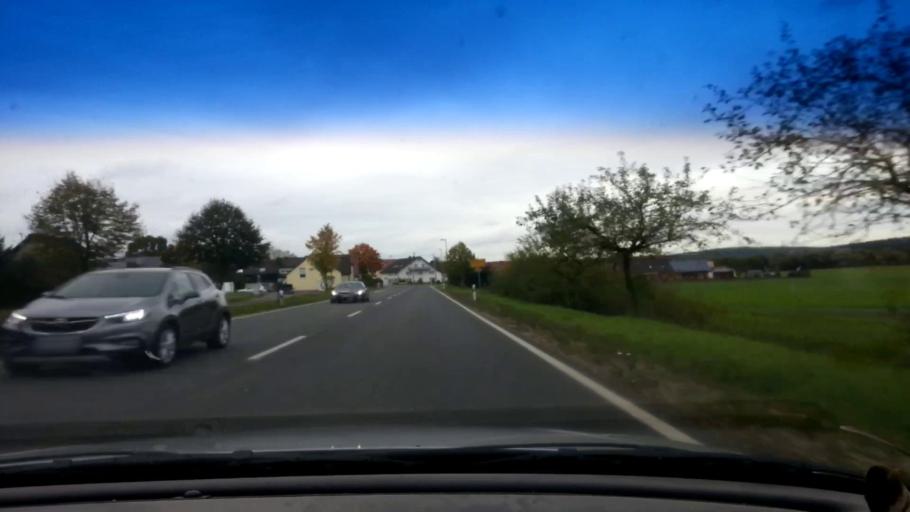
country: DE
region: Bavaria
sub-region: Upper Franconia
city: Reckendorf
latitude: 50.0149
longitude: 10.8273
